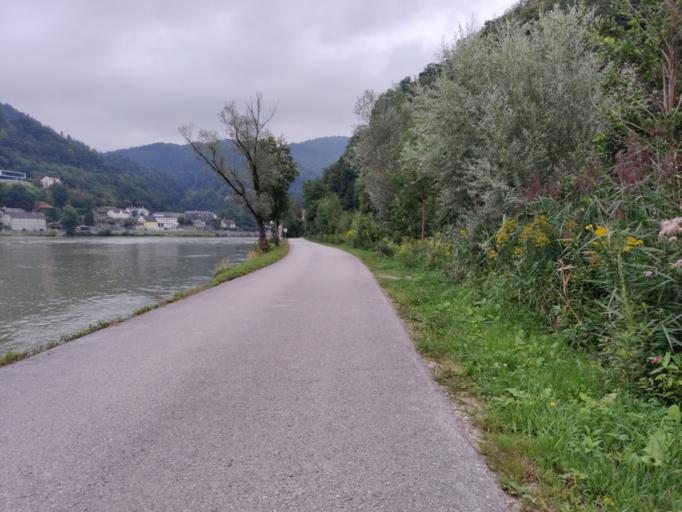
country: AT
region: Lower Austria
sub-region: Politischer Bezirk Melk
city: Nochling
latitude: 48.2284
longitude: 14.9002
